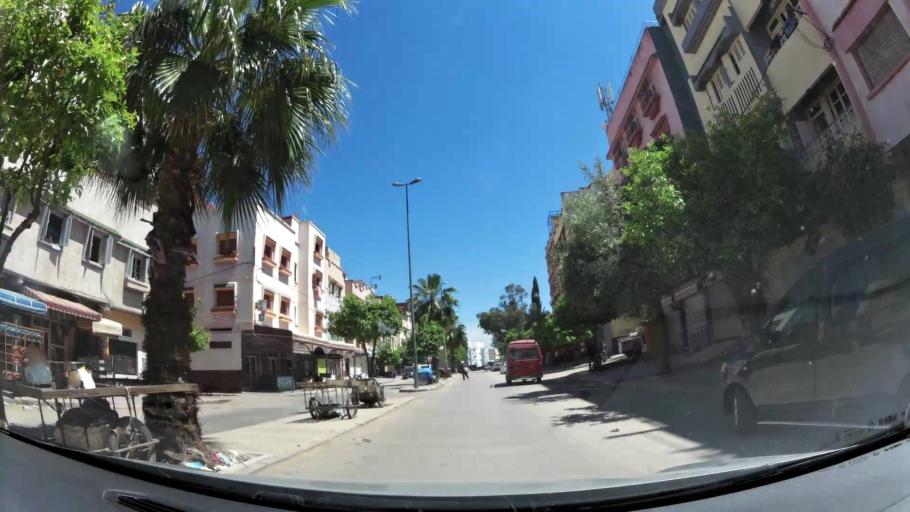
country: MA
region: Meknes-Tafilalet
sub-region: Meknes
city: Meknes
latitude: 33.8972
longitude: -5.5767
